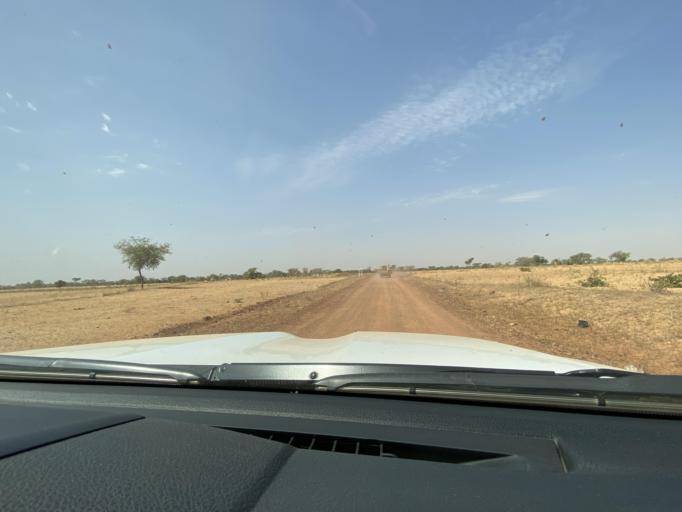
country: NE
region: Dosso
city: Birnin Gaoure
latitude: 13.2440
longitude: 2.8637
